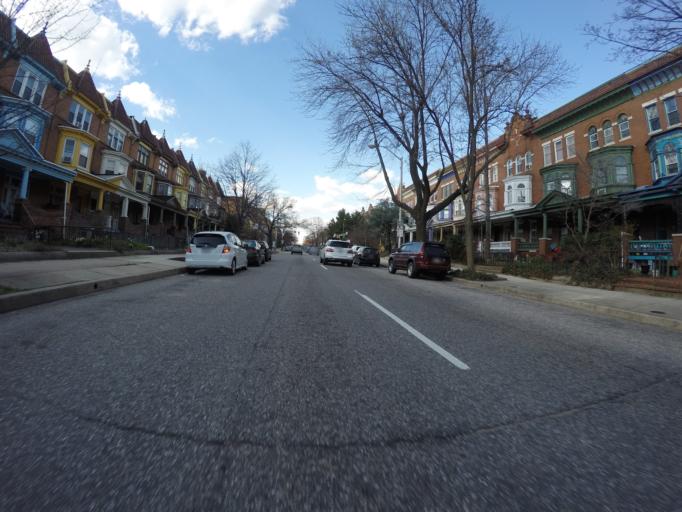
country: US
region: Maryland
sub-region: City of Baltimore
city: Baltimore
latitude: 39.3210
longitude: -76.6144
